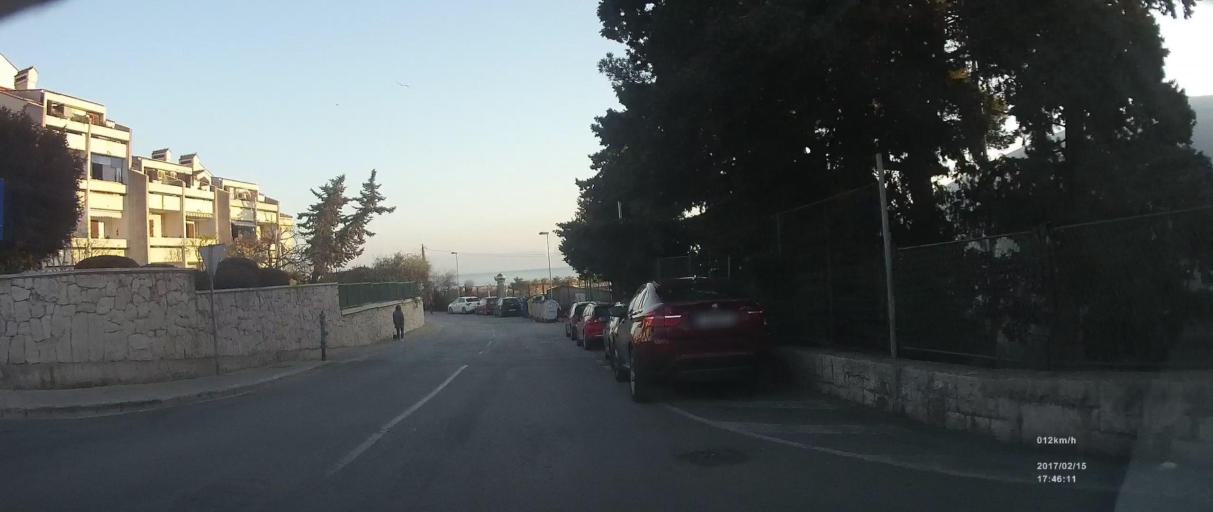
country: HR
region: Splitsko-Dalmatinska
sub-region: Grad Split
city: Split
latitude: 43.5017
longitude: 16.4572
